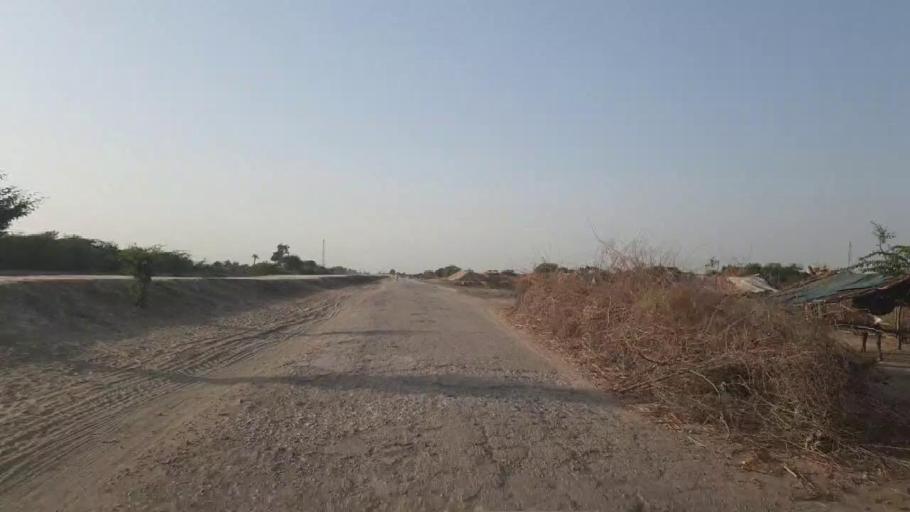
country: PK
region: Sindh
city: Dhoro Naro
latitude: 25.4917
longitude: 69.5659
